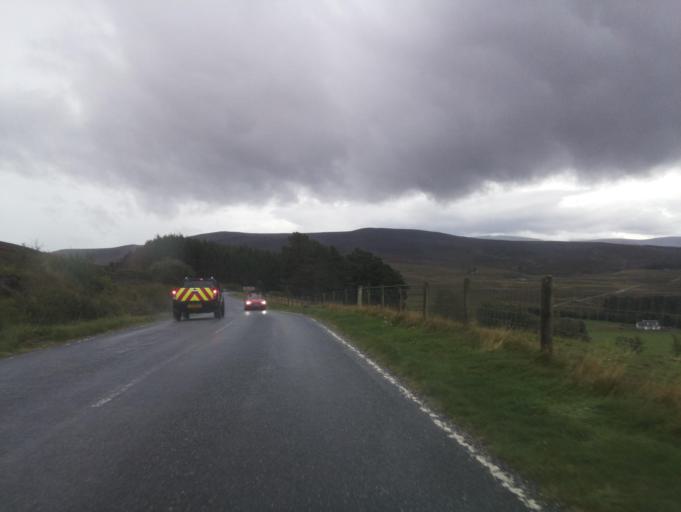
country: GB
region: Scotland
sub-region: Highland
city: Grantown on Spey
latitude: 57.2754
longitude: -3.5517
